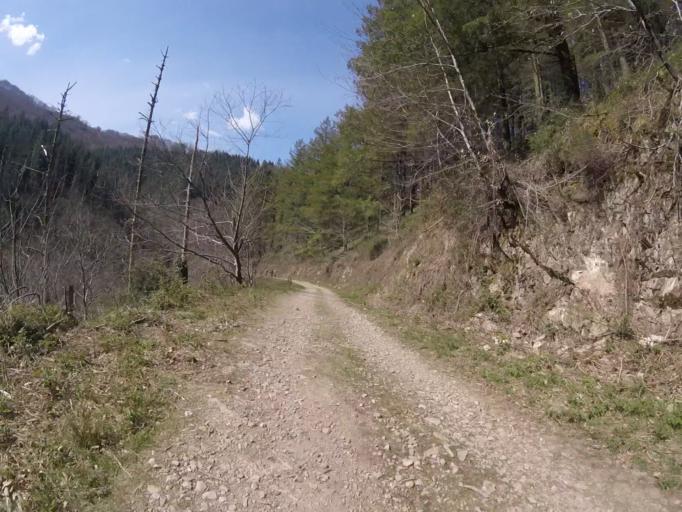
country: ES
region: Basque Country
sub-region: Provincia de Guipuzcoa
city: Irun
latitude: 43.2553
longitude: -1.8061
